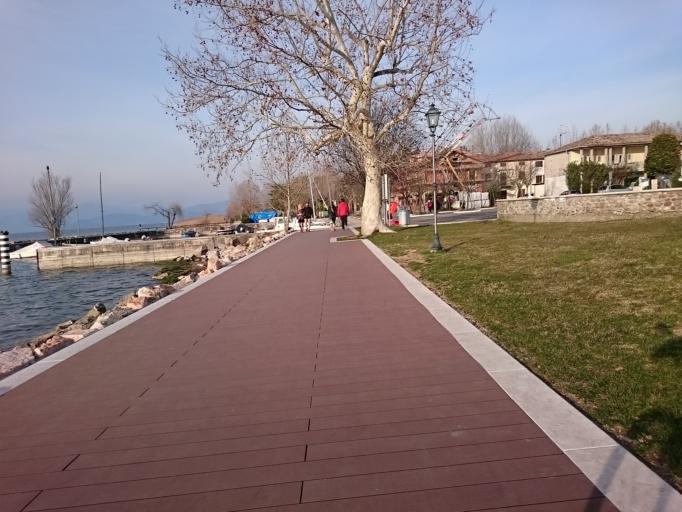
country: IT
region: Veneto
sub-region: Provincia di Verona
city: Peschiera del Garda
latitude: 45.4521
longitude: 10.6975
